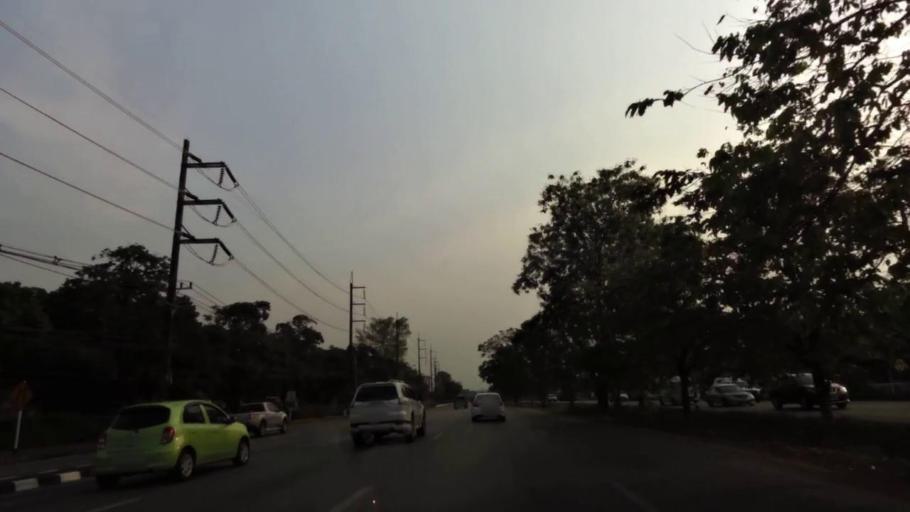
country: TH
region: Chanthaburi
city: Khlung
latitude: 12.5104
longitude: 102.1692
